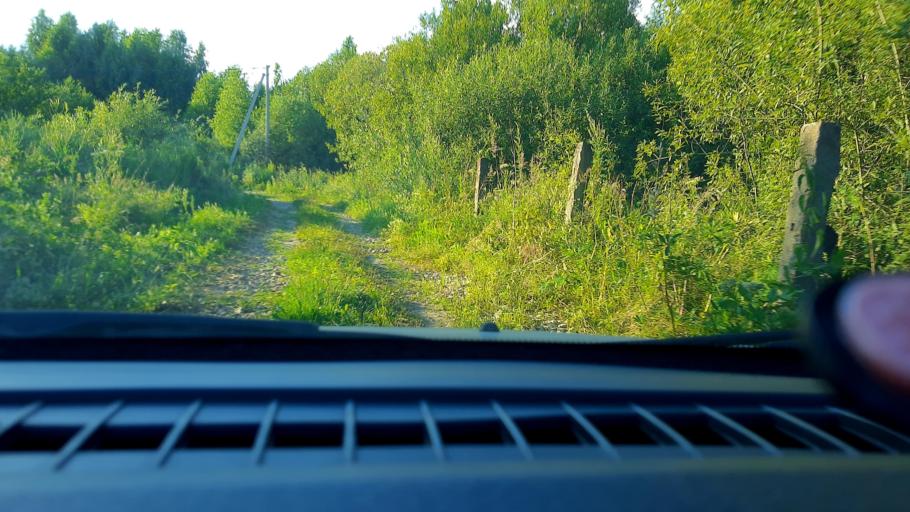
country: RU
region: Nizjnij Novgorod
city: Burevestnik
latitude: 56.0470
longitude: 43.8827
